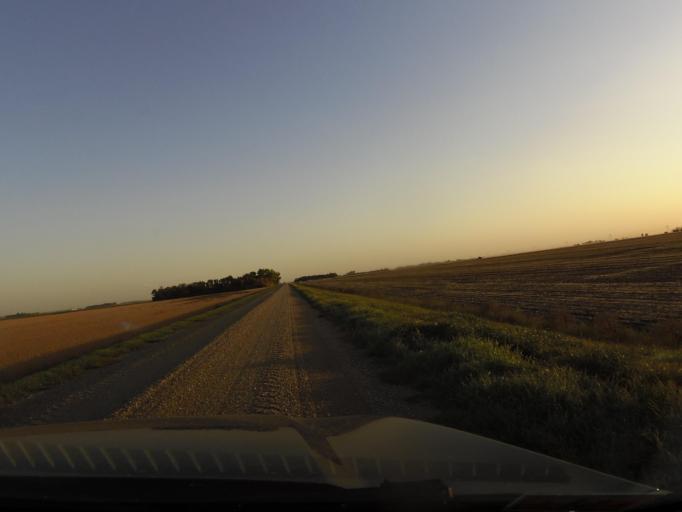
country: US
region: North Dakota
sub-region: Walsh County
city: Grafton
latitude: 48.3952
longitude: -97.2556
